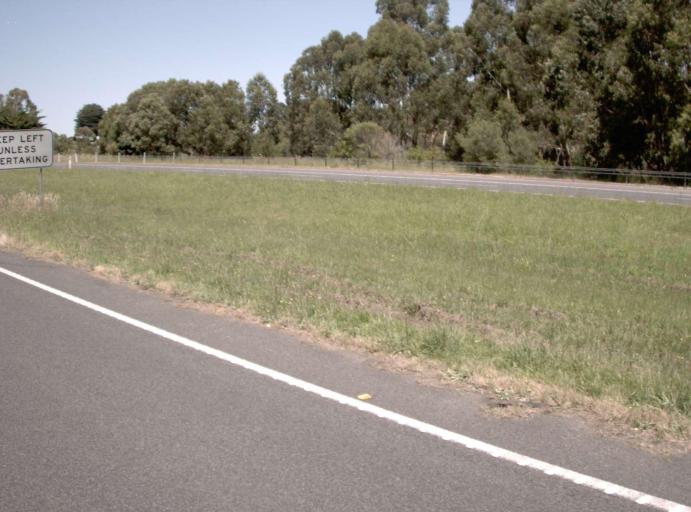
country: AU
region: Victoria
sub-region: Baw Baw
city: Warragul
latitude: -38.1393
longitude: 145.8837
